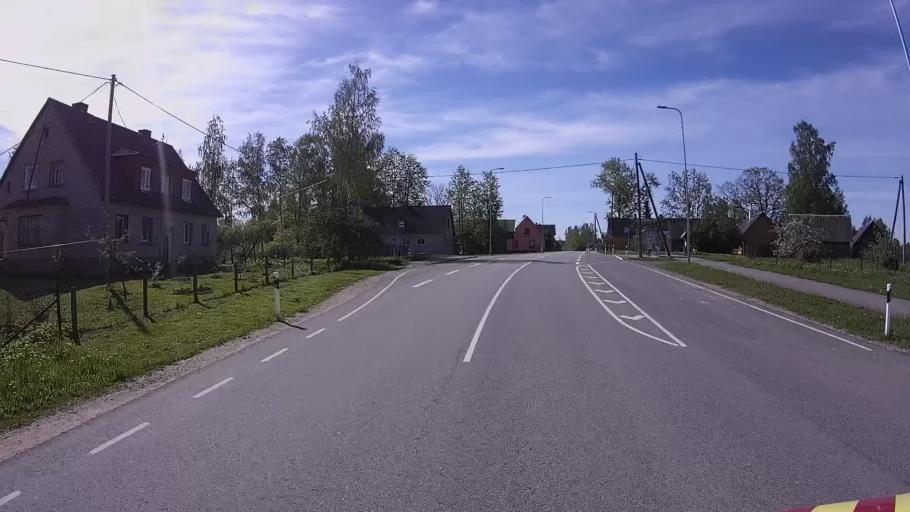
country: EE
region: Polvamaa
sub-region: Raepina vald
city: Rapina
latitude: 58.0057
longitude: 27.5426
